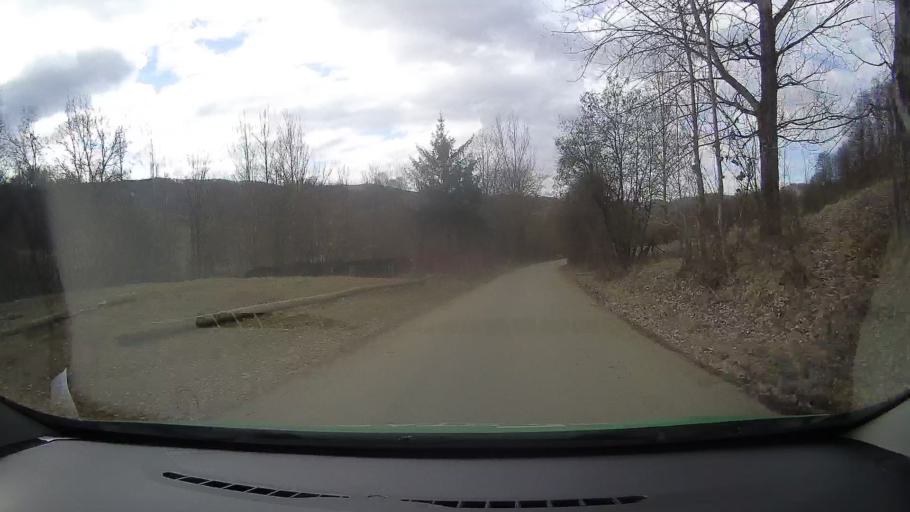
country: RO
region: Prahova
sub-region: Comuna Adunati
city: Adunati
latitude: 45.1203
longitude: 25.5977
